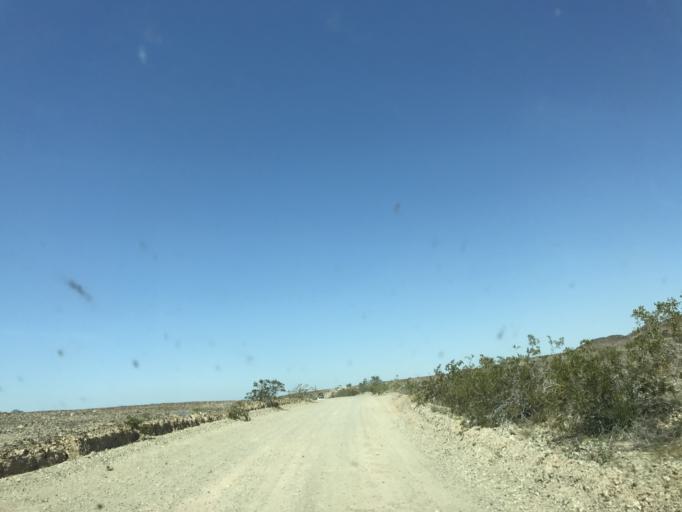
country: US
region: California
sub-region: Riverside County
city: Mesa Verde
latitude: 33.4977
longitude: -114.8463
